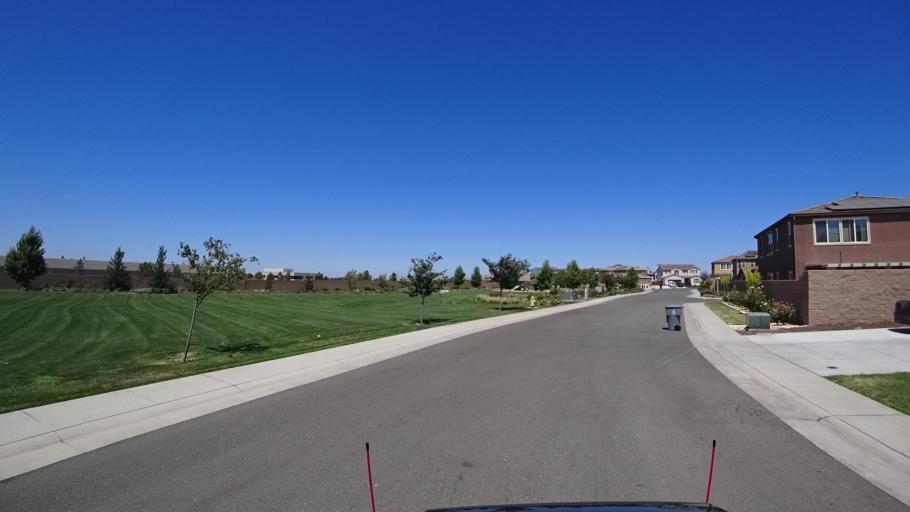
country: US
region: California
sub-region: Placer County
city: Rocklin
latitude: 38.8149
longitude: -121.2809
